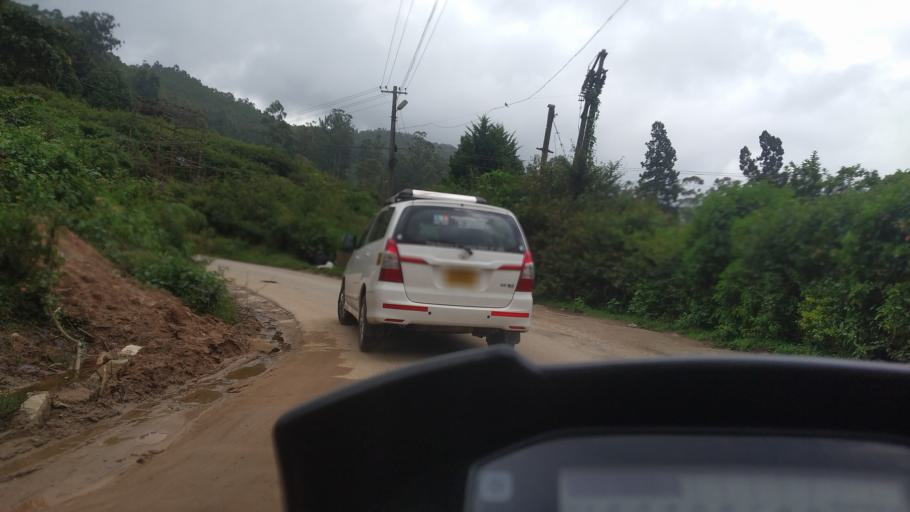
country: IN
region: Kerala
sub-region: Idukki
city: Munnar
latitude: 10.0676
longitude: 77.1064
